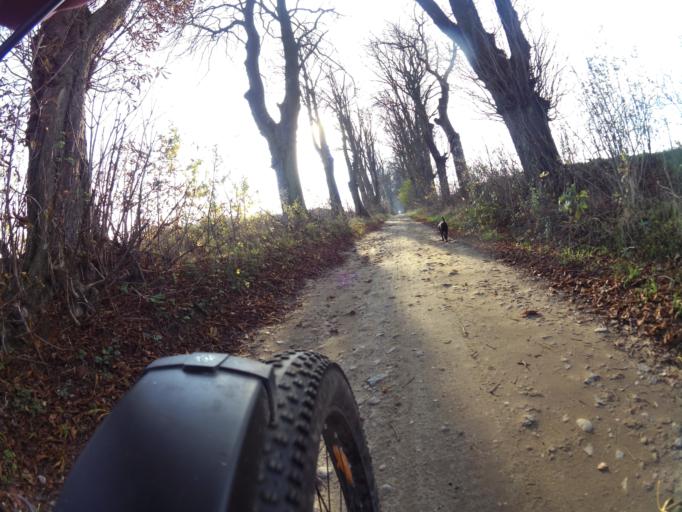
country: PL
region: Pomeranian Voivodeship
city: Strzelno
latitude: 54.7561
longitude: 18.2915
